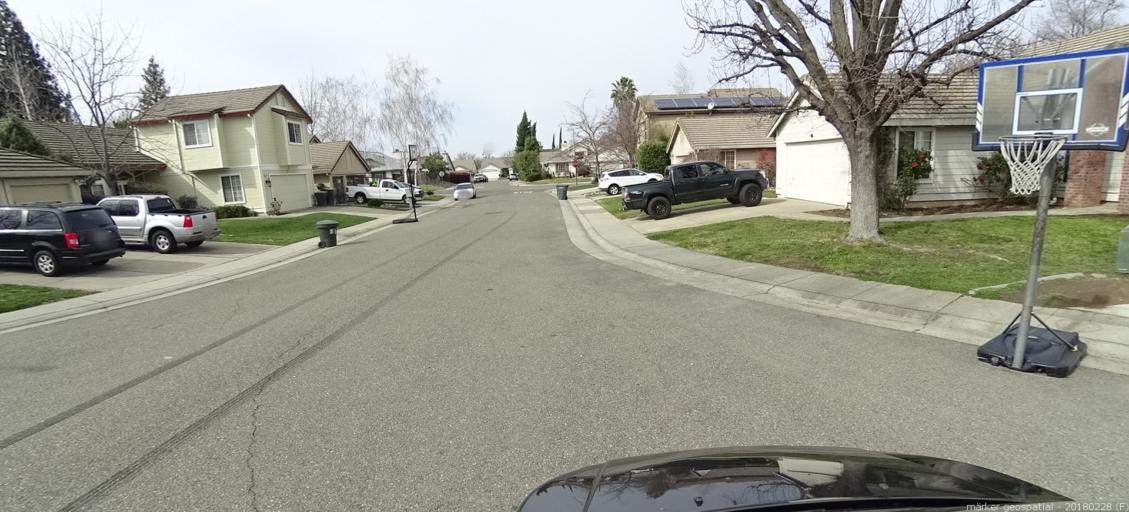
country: US
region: California
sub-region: Sacramento County
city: Antelope
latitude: 38.7170
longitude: -121.3380
